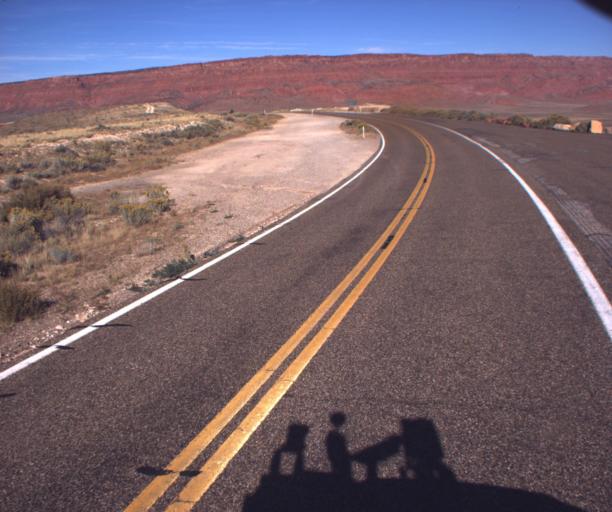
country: US
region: Arizona
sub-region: Coconino County
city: Fredonia
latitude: 36.7230
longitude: -112.0604
